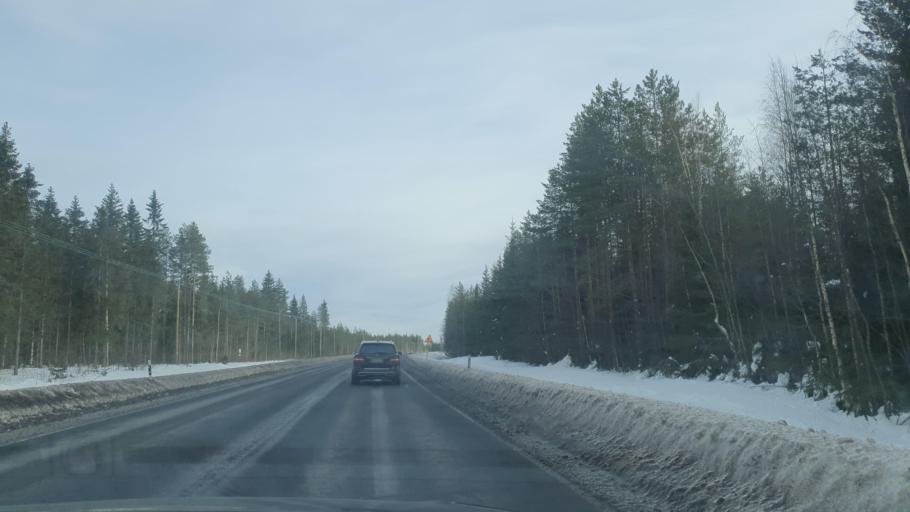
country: FI
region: Northern Ostrobothnia
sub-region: Oulu
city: Muhos
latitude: 64.7870
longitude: 26.1756
